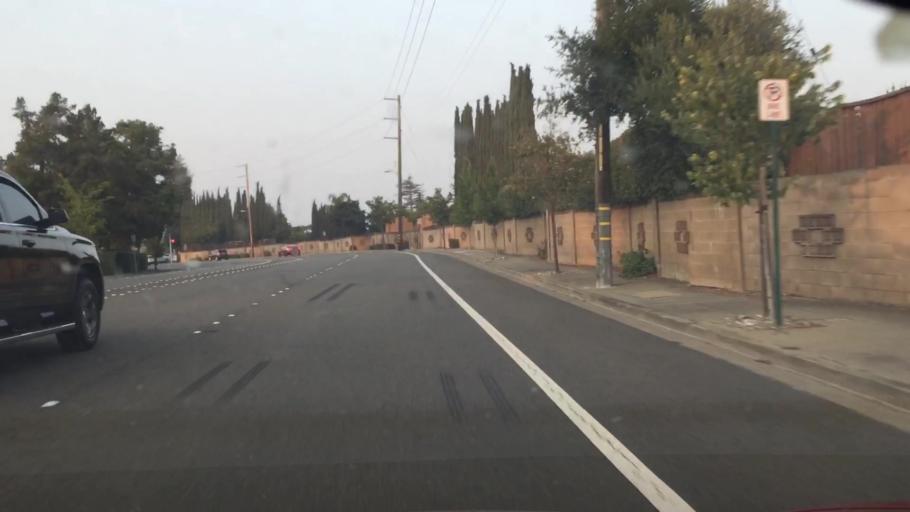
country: US
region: California
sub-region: Alameda County
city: Livermore
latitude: 37.6595
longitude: -121.7814
